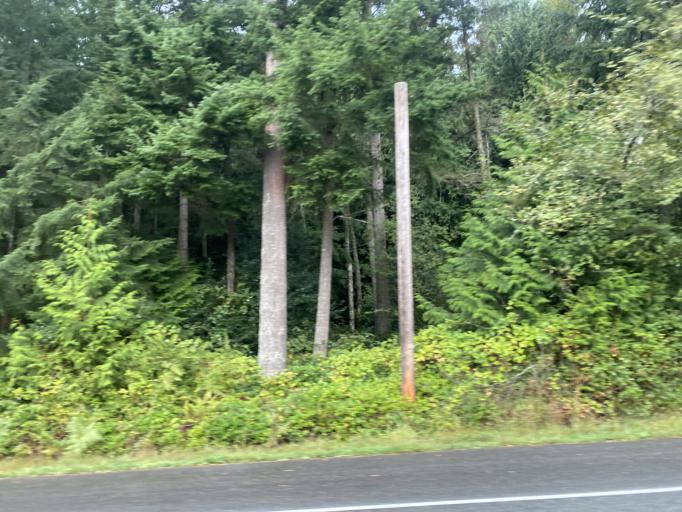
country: US
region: Washington
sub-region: Island County
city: Langley
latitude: 48.0051
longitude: -122.4123
